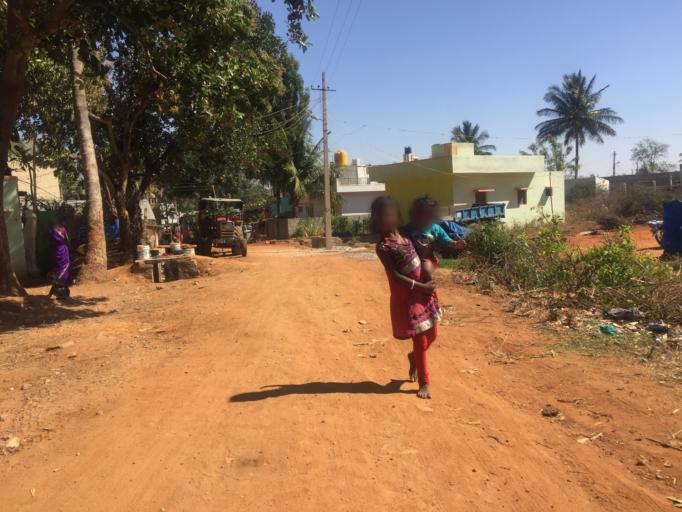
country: IN
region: Karnataka
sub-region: Chikkaballapur
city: Chik Ballapur
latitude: 13.3817
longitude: 77.6828
